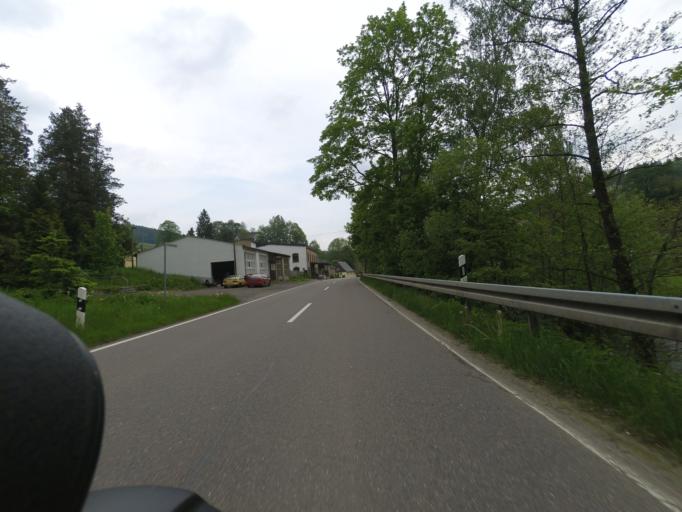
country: DE
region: Saxony
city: Drebach
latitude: 50.6777
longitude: 13.0558
